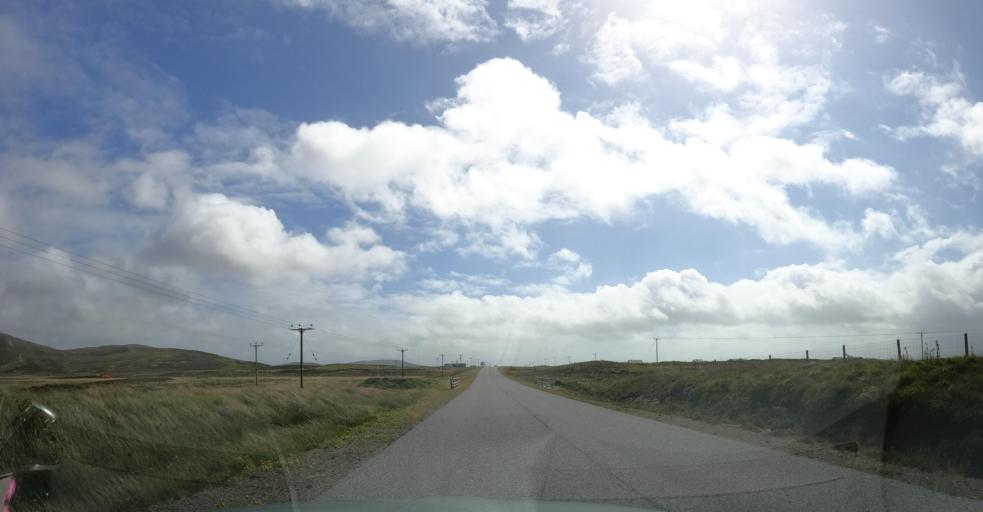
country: GB
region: Scotland
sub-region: Eilean Siar
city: Isle of South Uist
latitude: 57.2280
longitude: -7.3971
